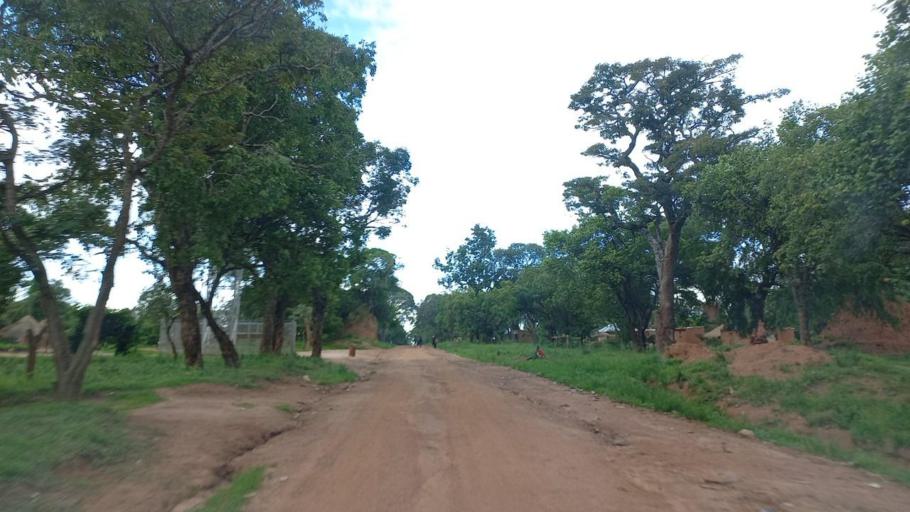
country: ZM
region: North-Western
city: Mwinilunga
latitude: -11.8455
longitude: 24.3638
